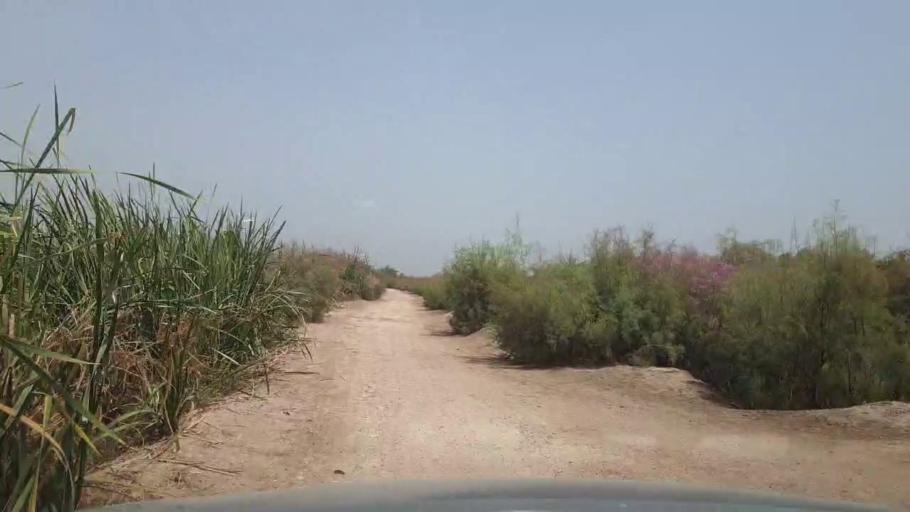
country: PK
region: Sindh
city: Garhi Yasin
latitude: 27.9507
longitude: 68.4345
